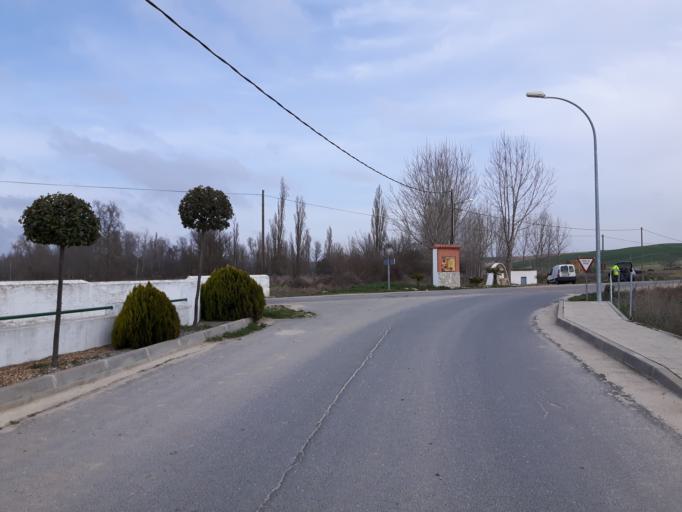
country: ES
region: Castille and Leon
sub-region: Provincia de Salamanca
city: Tordillos
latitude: 40.8556
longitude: -5.3522
